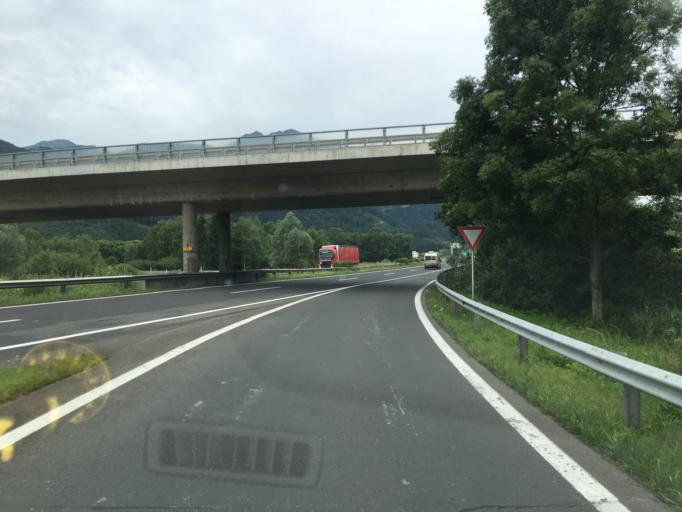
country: AT
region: Styria
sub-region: Politischer Bezirk Liezen
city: Trieben
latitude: 47.4959
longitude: 14.4819
